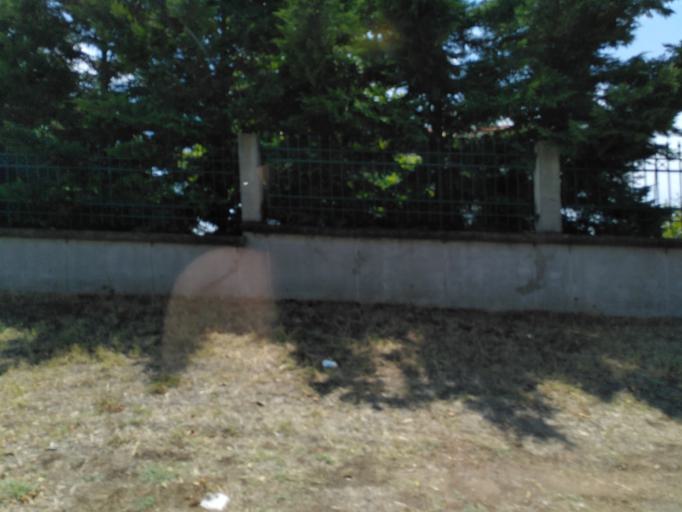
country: GR
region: Central Macedonia
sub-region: Nomos Thessalonikis
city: Epanomi
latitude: 40.4320
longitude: 22.9140
